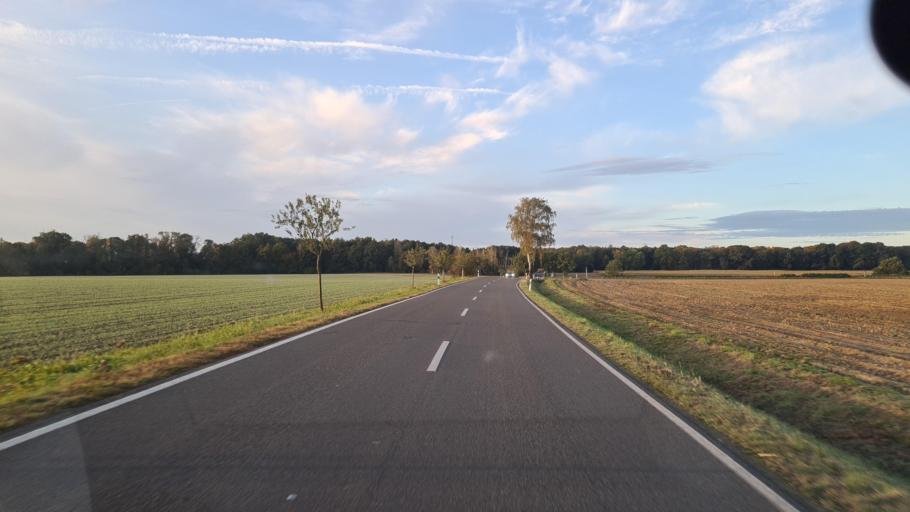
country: DE
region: Saxony
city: Machern
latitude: 51.3758
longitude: 12.6474
